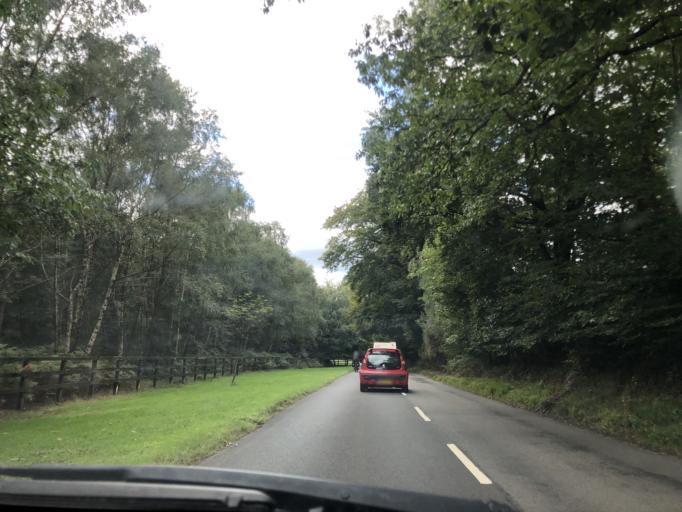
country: GB
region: England
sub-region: East Sussex
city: Forest Row
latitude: 51.0731
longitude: 0.0347
